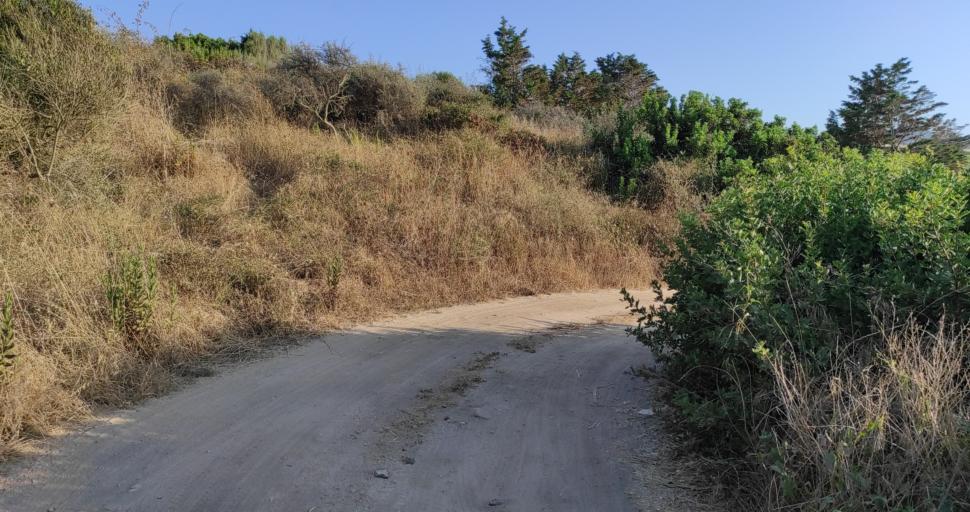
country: FR
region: Corsica
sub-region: Departement de la Corse-du-Sud
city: Alata
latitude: 41.9850
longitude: 8.6715
